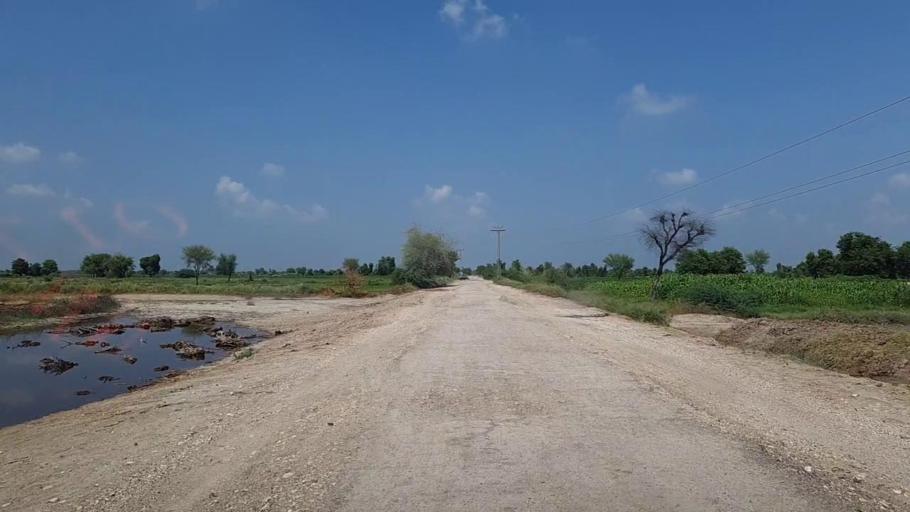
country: PK
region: Sindh
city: Kandiaro
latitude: 27.0126
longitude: 68.2647
